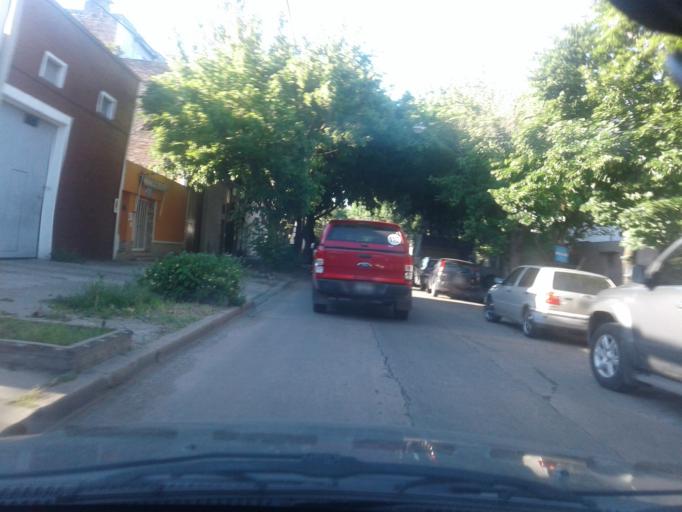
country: AR
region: Santa Fe
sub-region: Departamento de Rosario
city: Rosario
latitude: -32.9449
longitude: -60.6863
